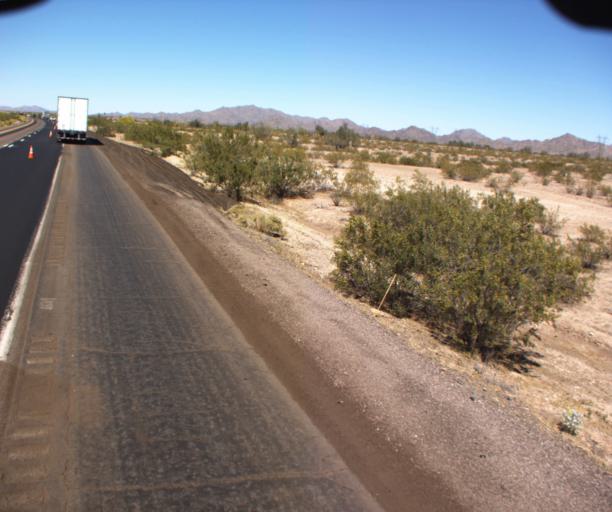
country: US
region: Arizona
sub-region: Maricopa County
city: Gila Bend
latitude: 33.0494
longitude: -112.6434
